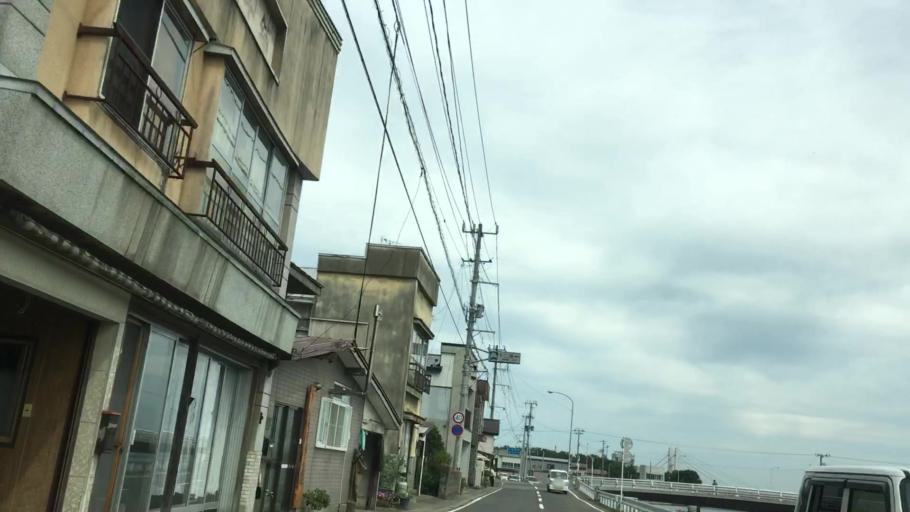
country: JP
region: Aomori
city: Shimokizukuri
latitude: 40.7762
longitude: 140.2167
